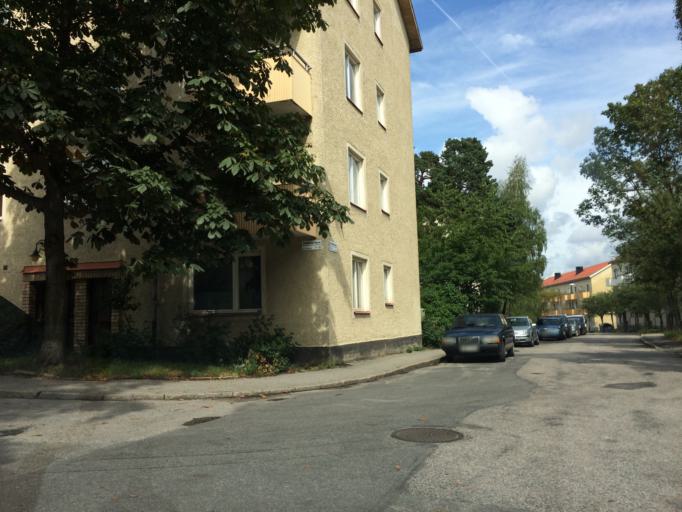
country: SE
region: Stockholm
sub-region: Stockholms Kommun
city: Arsta
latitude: 59.2959
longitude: 18.0083
